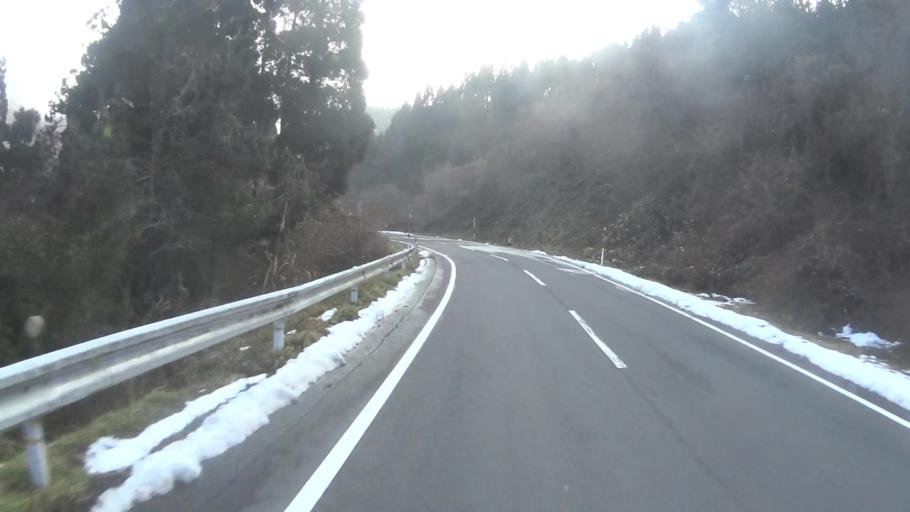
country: JP
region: Kyoto
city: Maizuru
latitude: 35.4187
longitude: 135.4093
